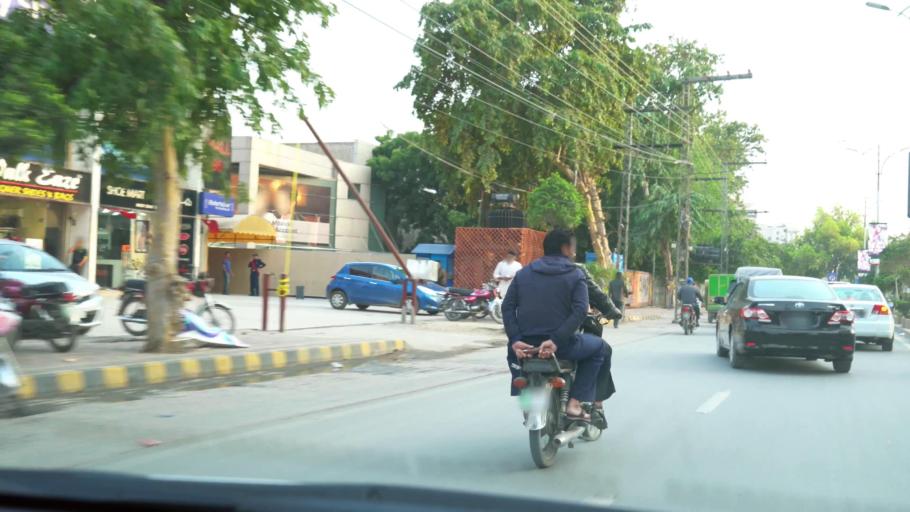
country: PK
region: Punjab
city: Lahore
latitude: 31.5089
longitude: 74.3504
